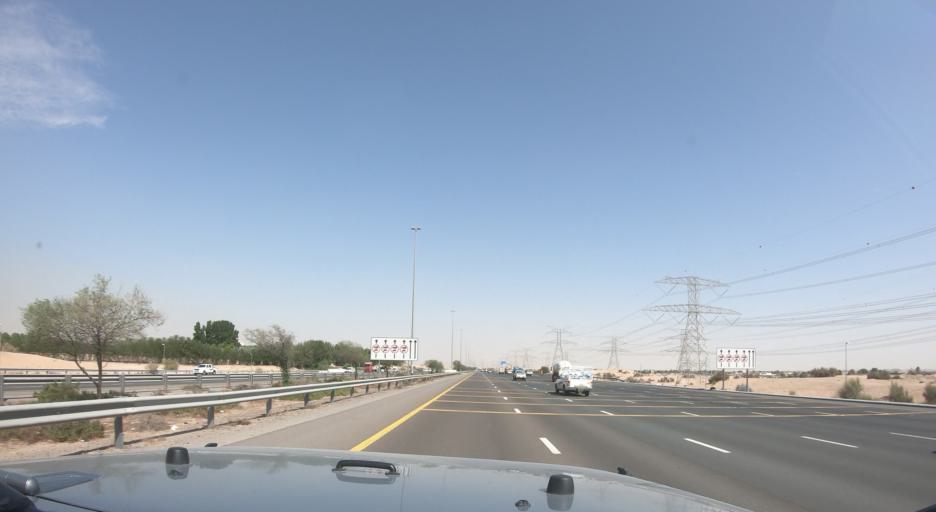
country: AE
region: Ash Shariqah
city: Sharjah
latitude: 25.1866
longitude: 55.5267
